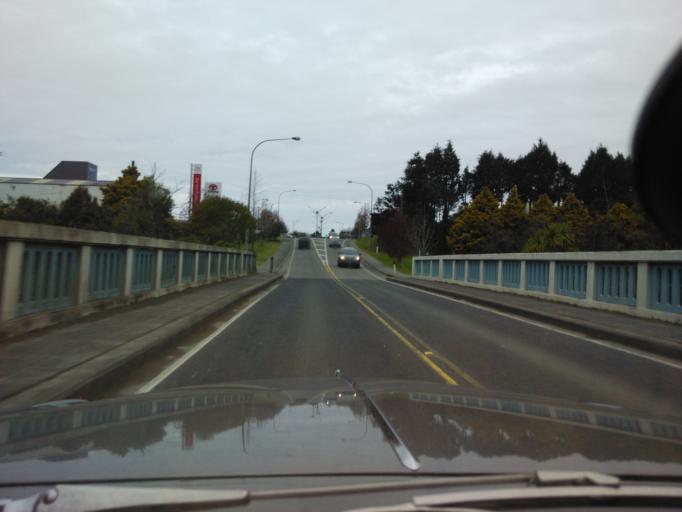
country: NZ
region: Auckland
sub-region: Auckland
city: Rothesay Bay
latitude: -36.7231
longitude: 174.6928
